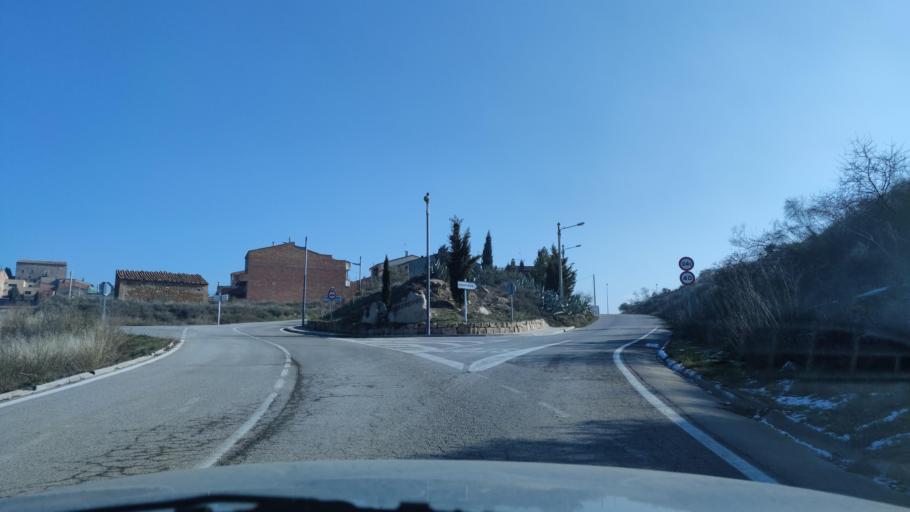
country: ES
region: Catalonia
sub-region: Provincia de Lleida
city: Torrebesses
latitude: 41.4261
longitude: 0.5903
